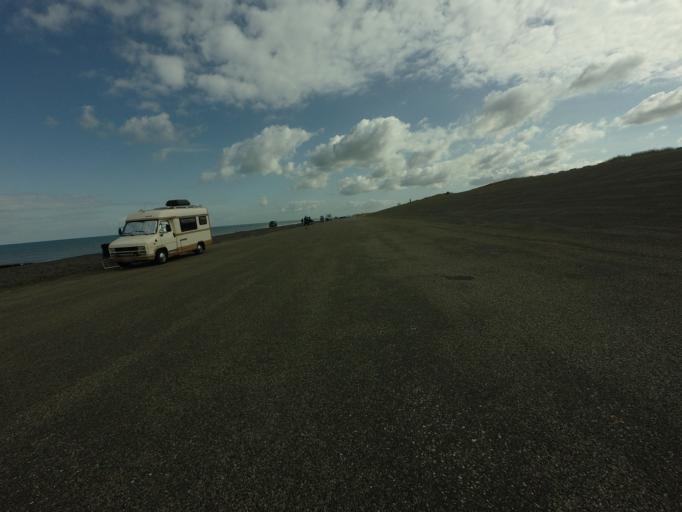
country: NL
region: Zeeland
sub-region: Gemeente Vlissingen
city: Vlissingen
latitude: 51.5465
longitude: 3.4503
